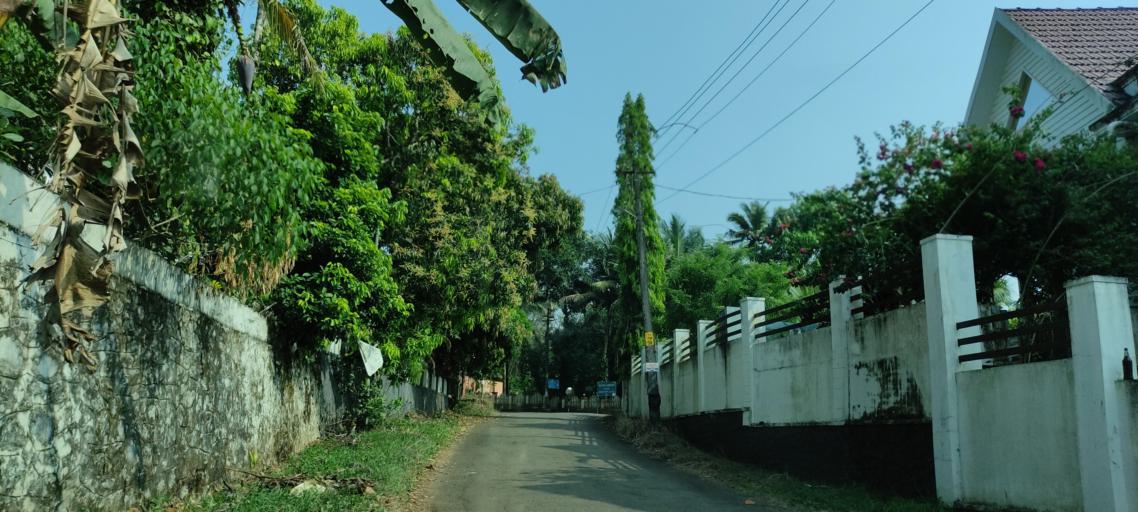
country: IN
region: Kerala
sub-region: Ernakulam
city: Piravam
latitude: 9.8190
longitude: 76.5176
